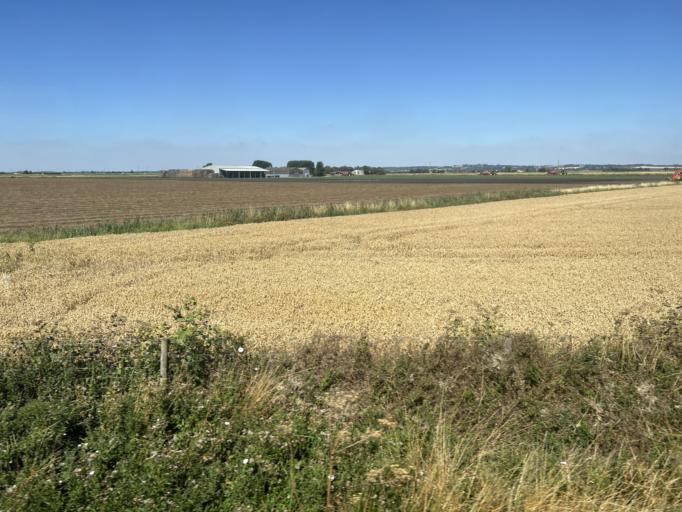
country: GB
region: England
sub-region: Lincolnshire
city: Spilsby
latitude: 53.1059
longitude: 0.1177
